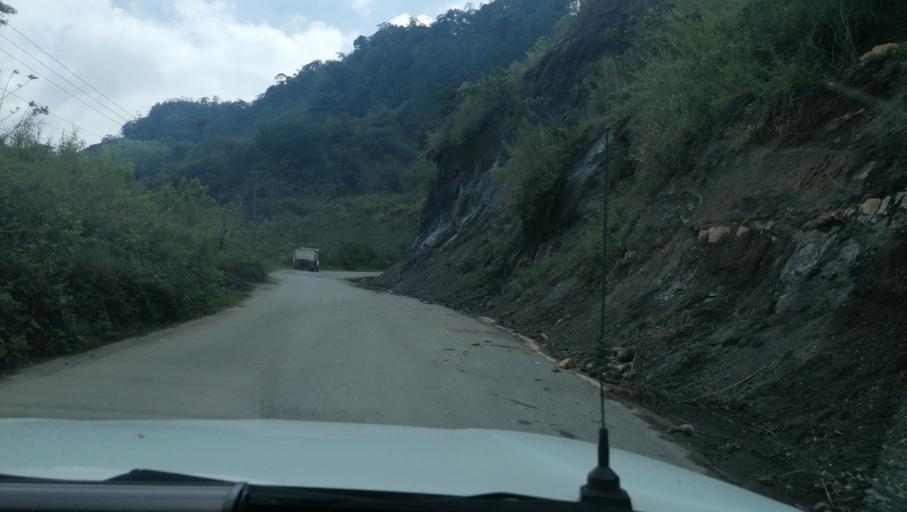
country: MX
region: Chiapas
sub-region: Ocotepec
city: San Pablo Huacano
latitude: 17.2612
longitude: -93.2677
